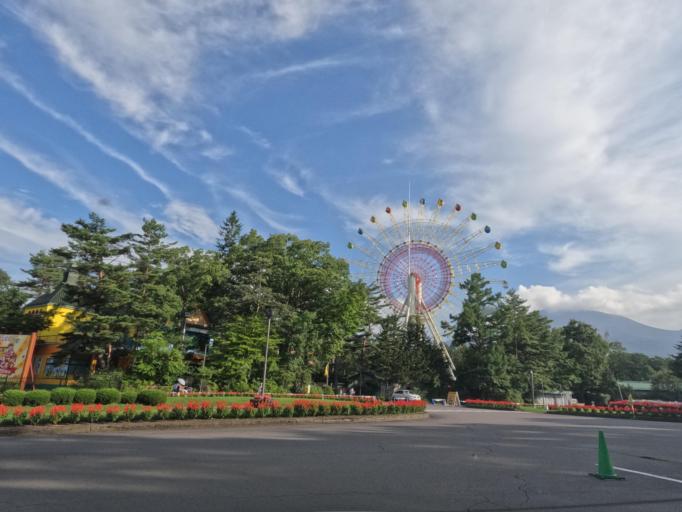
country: JP
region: Nagano
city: Komoro
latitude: 36.4743
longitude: 138.5440
